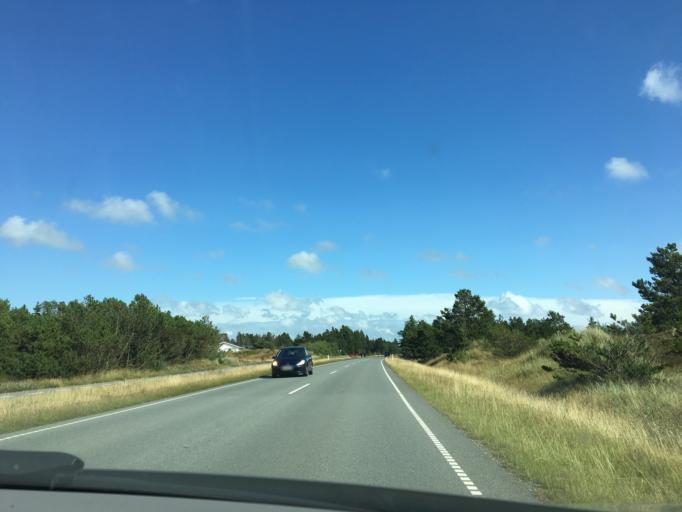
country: DK
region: South Denmark
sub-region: Varde Kommune
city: Oksbol
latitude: 55.7334
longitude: 8.1990
